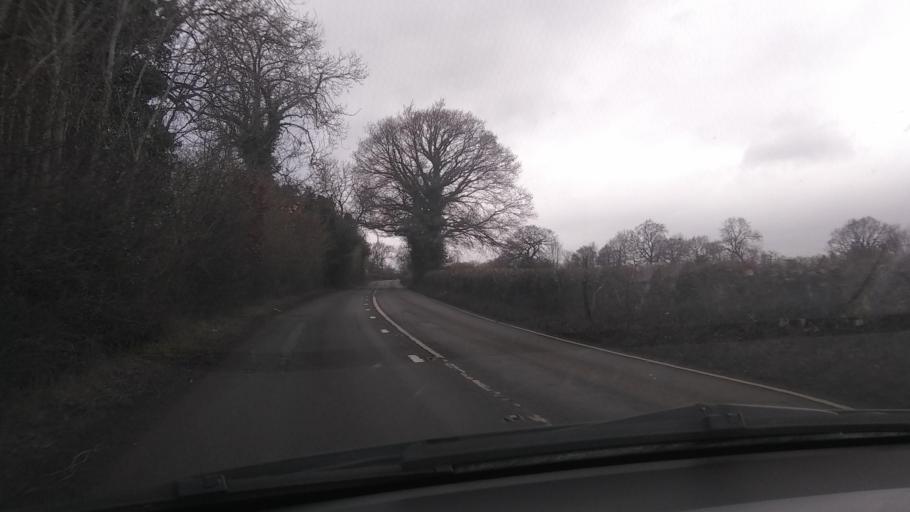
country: GB
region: England
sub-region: Shropshire
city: Cleobury Mortimer
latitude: 52.3838
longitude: -2.5389
